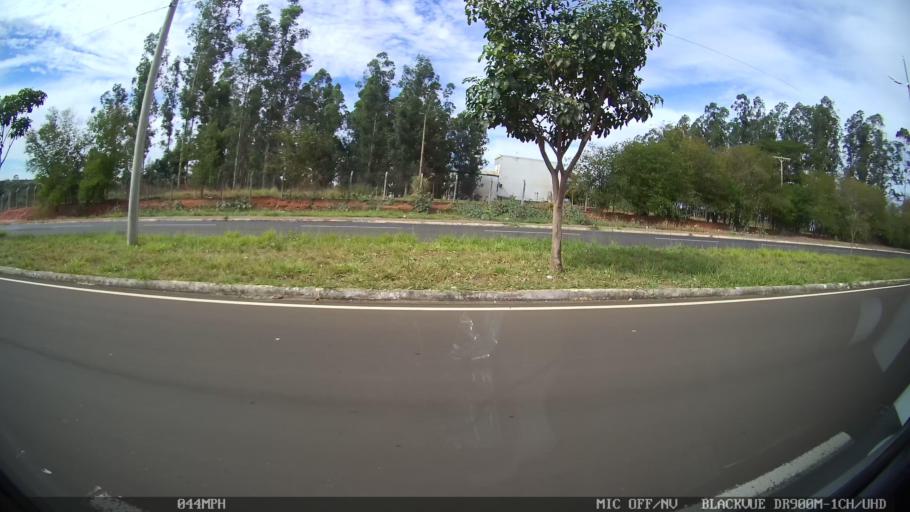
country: BR
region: Sao Paulo
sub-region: Catanduva
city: Catanduva
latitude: -21.1538
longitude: -48.9539
